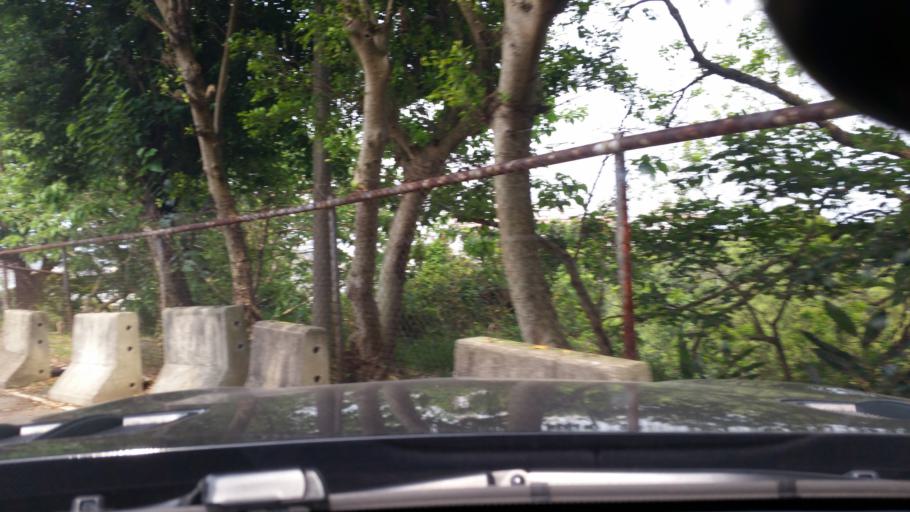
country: TW
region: Taiwan
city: Taoyuan City
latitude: 25.0660
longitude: 121.2939
